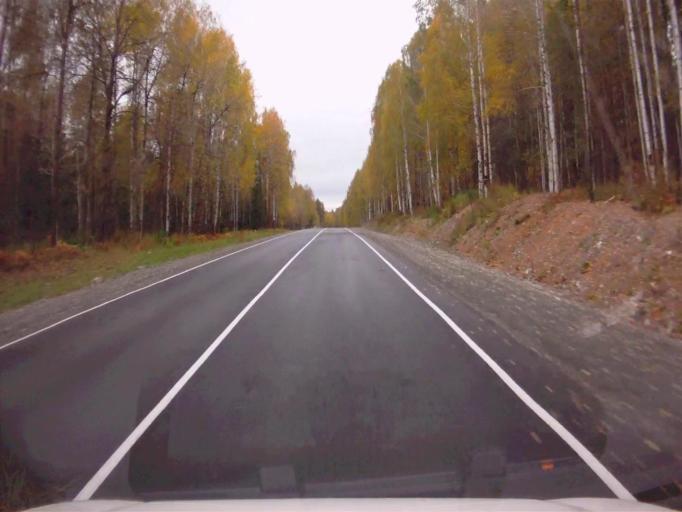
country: RU
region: Chelyabinsk
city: Nyazepetrovsk
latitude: 56.0635
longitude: 59.7052
